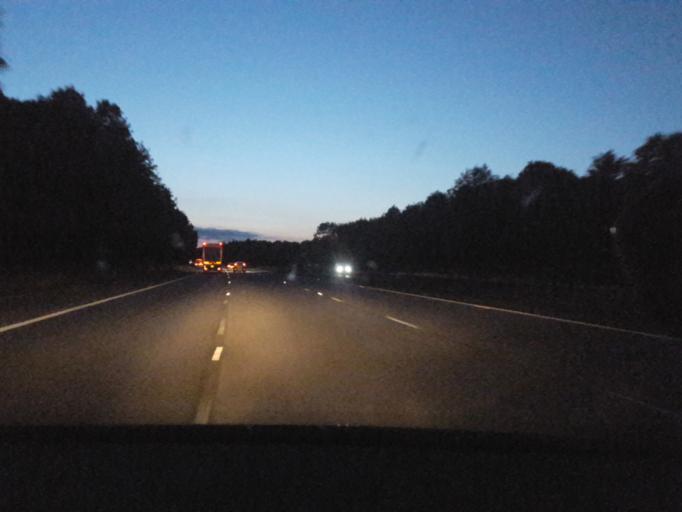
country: GB
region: England
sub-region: Leicestershire
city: Kirby Muxloe
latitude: 52.6525
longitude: -1.2395
